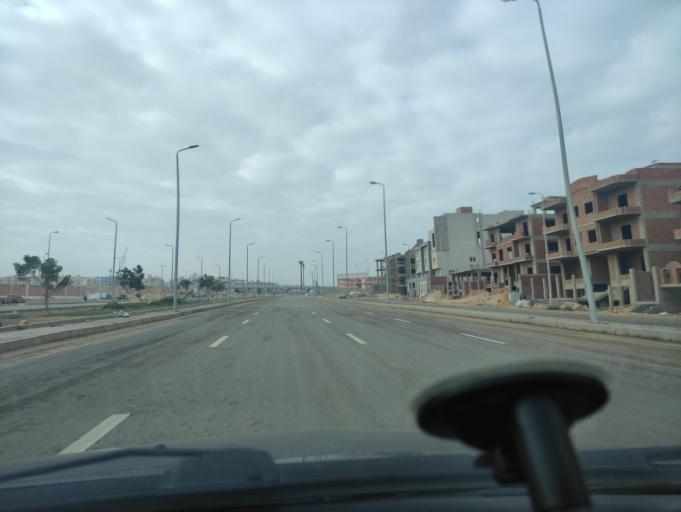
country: EG
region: Muhafazat al Qalyubiyah
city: Al Khankah
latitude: 30.0472
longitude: 31.5276
